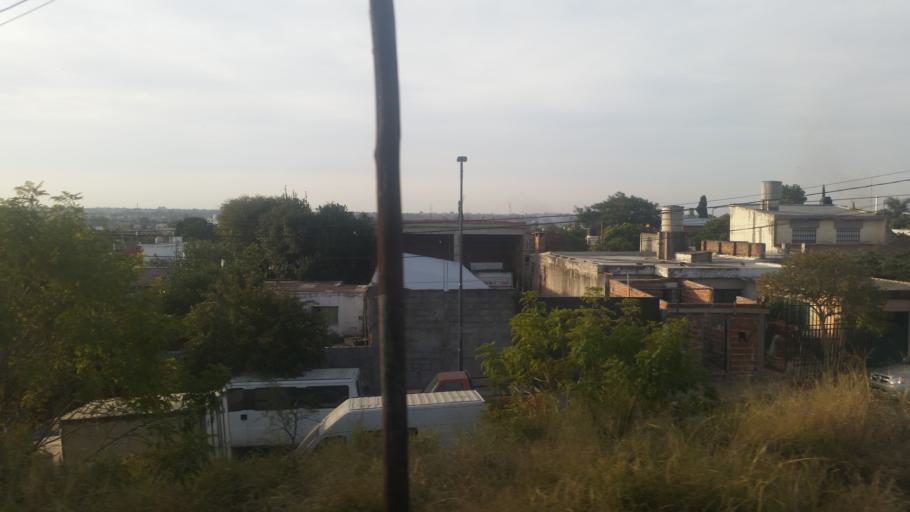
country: AR
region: Cordoba
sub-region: Departamento de Capital
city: Cordoba
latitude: -31.4317
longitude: -64.1449
